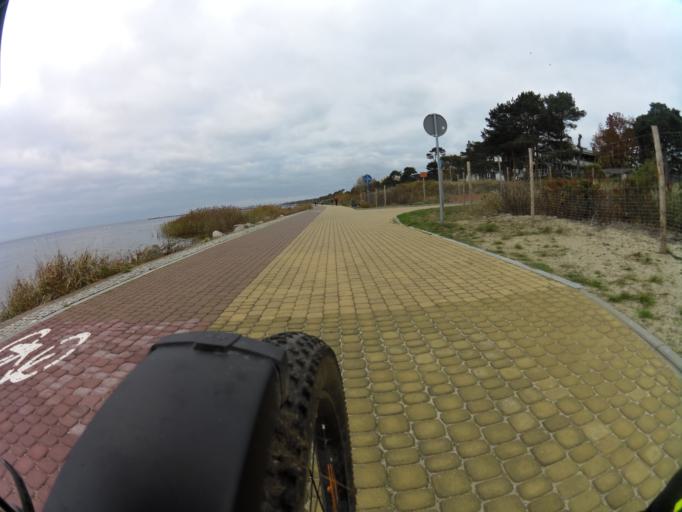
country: PL
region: Pomeranian Voivodeship
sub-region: Powiat pucki
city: Jastarnia
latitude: 54.6779
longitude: 18.7162
